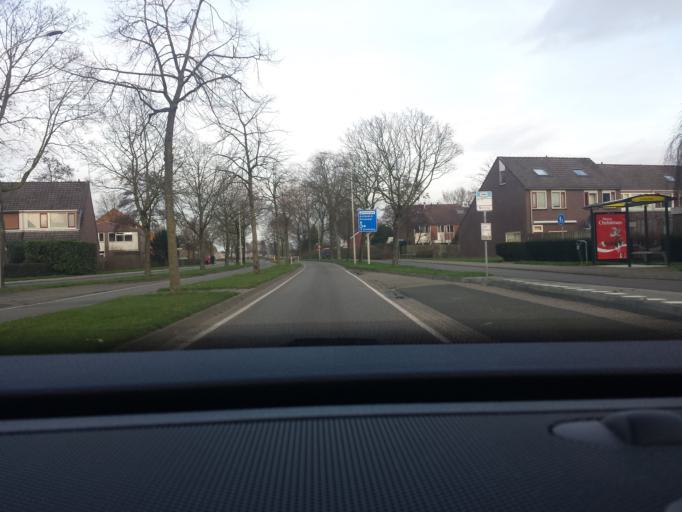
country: NL
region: Gelderland
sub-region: Gemeente Duiven
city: Duiven
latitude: 51.9466
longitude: 6.0288
